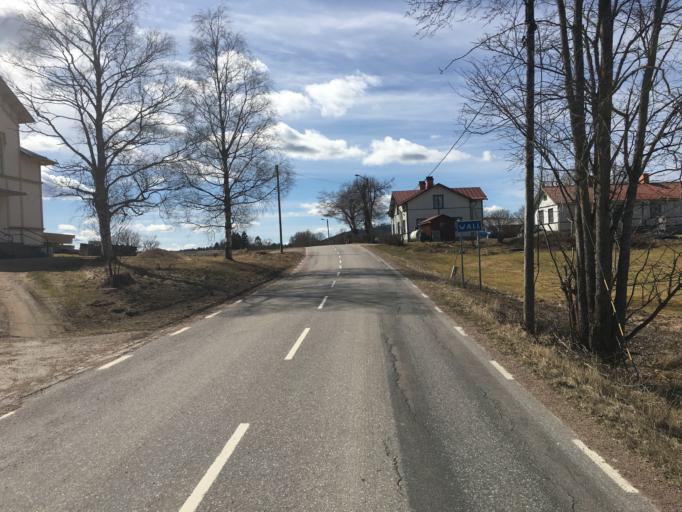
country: SE
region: Gaevleborg
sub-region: Hofors Kommun
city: Hofors
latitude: 60.5082
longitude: 16.4594
